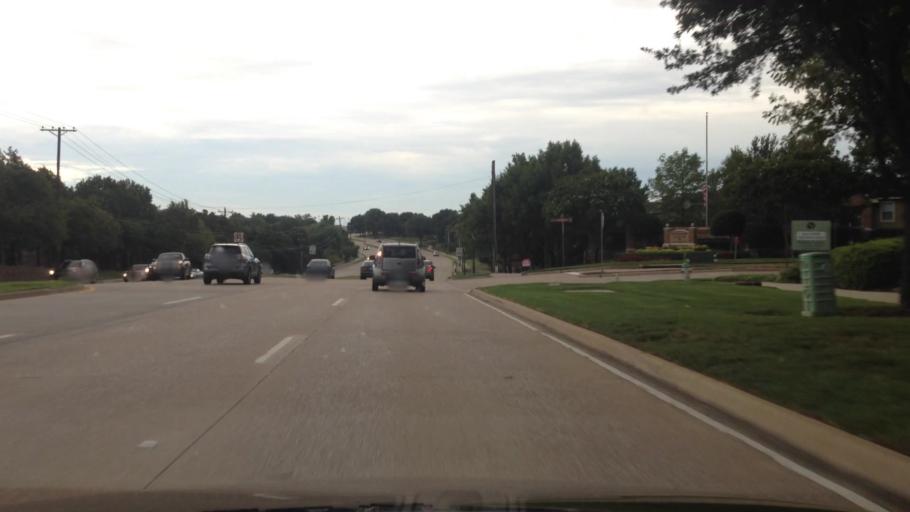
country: US
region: Texas
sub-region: Denton County
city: Flower Mound
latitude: 33.0089
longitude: -97.0452
